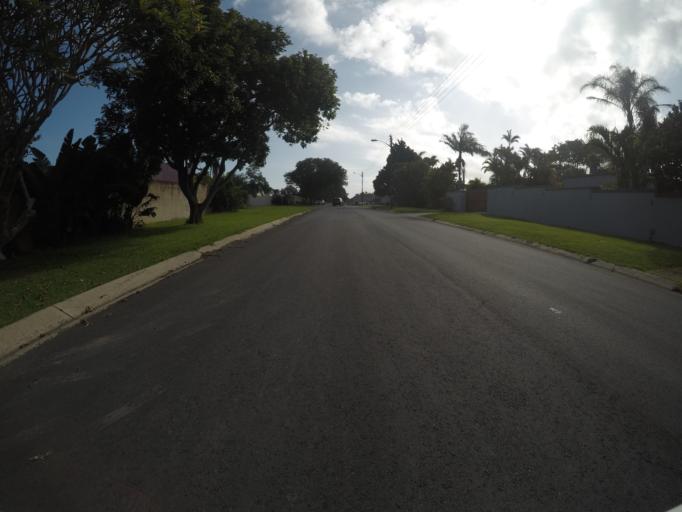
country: ZA
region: Eastern Cape
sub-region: Buffalo City Metropolitan Municipality
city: East London
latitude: -32.9692
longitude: 27.9517
